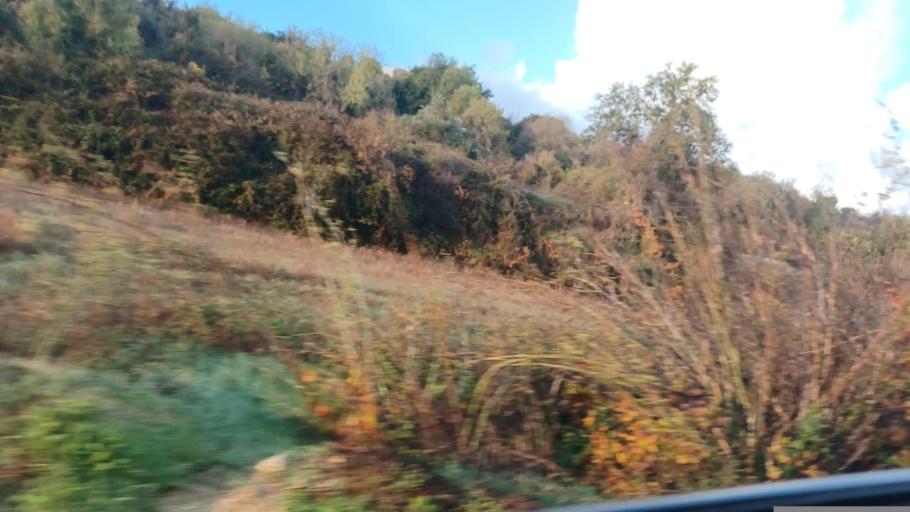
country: CY
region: Pafos
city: Mesogi
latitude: 34.8456
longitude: 32.5258
